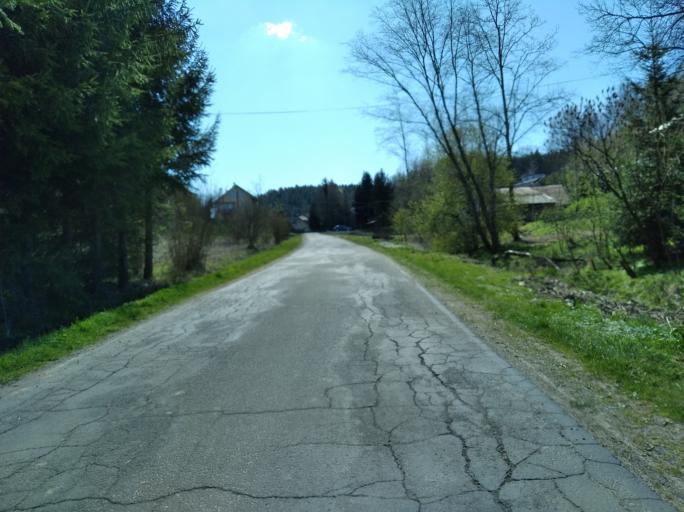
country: PL
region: Subcarpathian Voivodeship
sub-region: Powiat brzozowski
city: Dydnia
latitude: 49.7298
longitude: 22.1501
